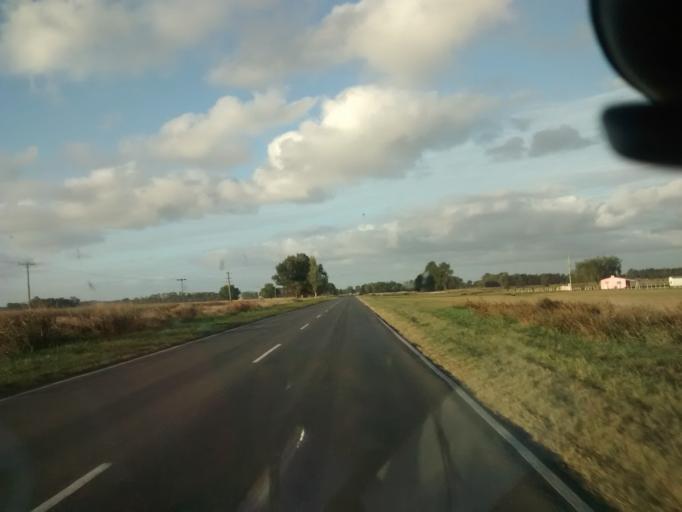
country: AR
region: Buenos Aires
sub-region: Partido de General Belgrano
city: General Belgrano
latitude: -35.7912
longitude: -58.5464
